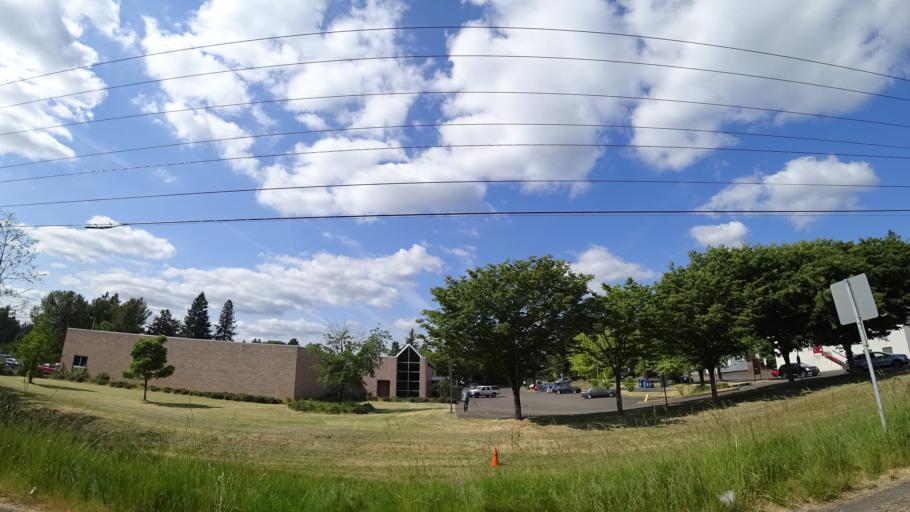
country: US
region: Oregon
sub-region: Washington County
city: Garden Home-Whitford
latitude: 45.4675
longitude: -122.7184
